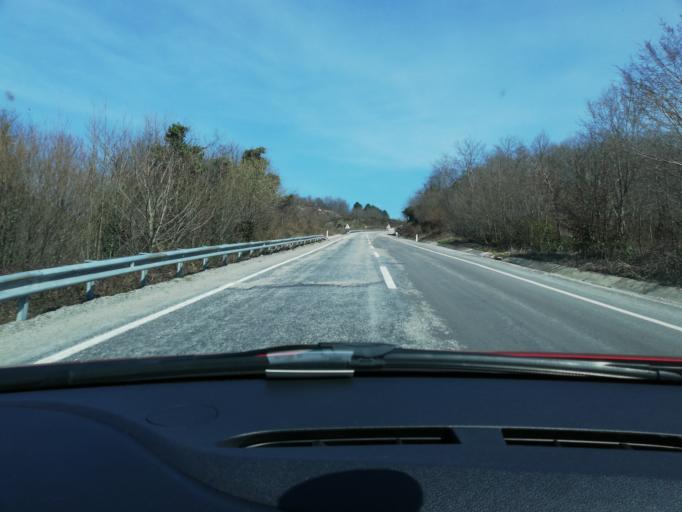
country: TR
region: Bartin
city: Amasra
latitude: 41.7266
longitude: 32.4051
